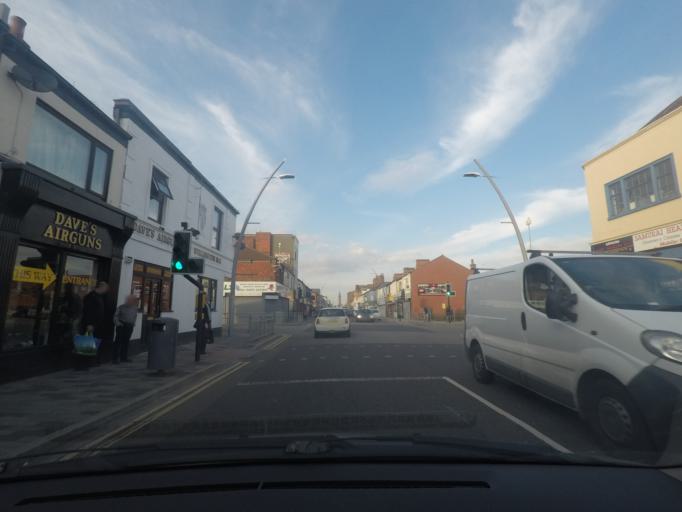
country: GB
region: England
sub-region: North East Lincolnshire
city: Grimsby
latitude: 53.5686
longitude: -0.0745
